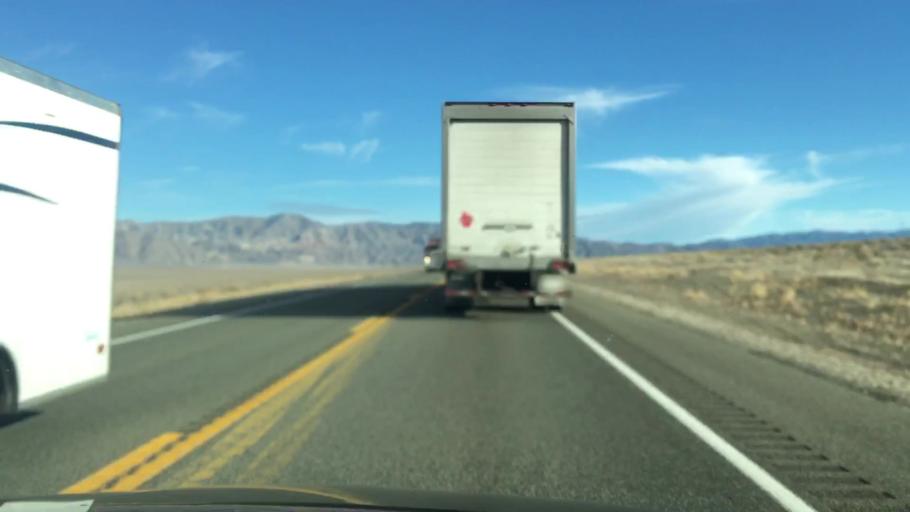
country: US
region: Nevada
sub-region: Mineral County
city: Hawthorne
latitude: 38.5316
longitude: -118.2774
